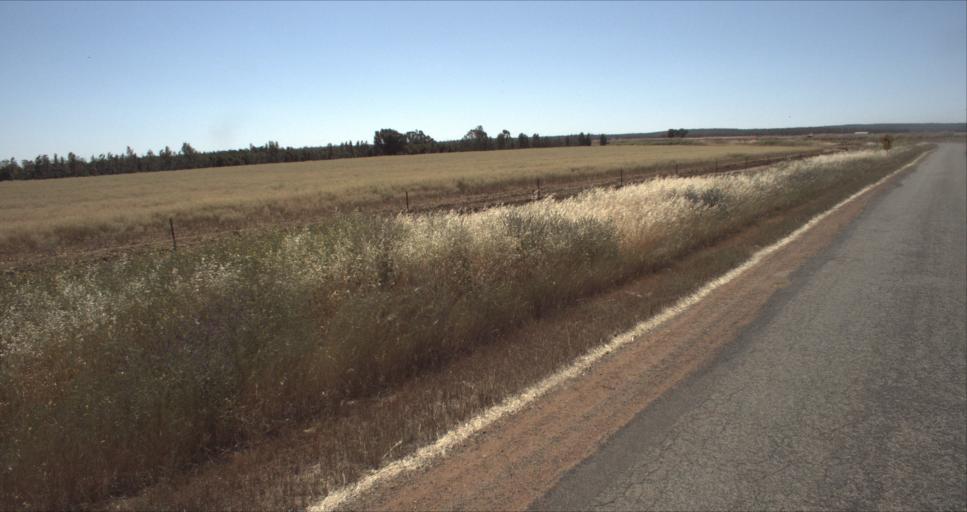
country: AU
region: New South Wales
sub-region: Leeton
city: Leeton
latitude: -34.4717
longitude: 146.4168
